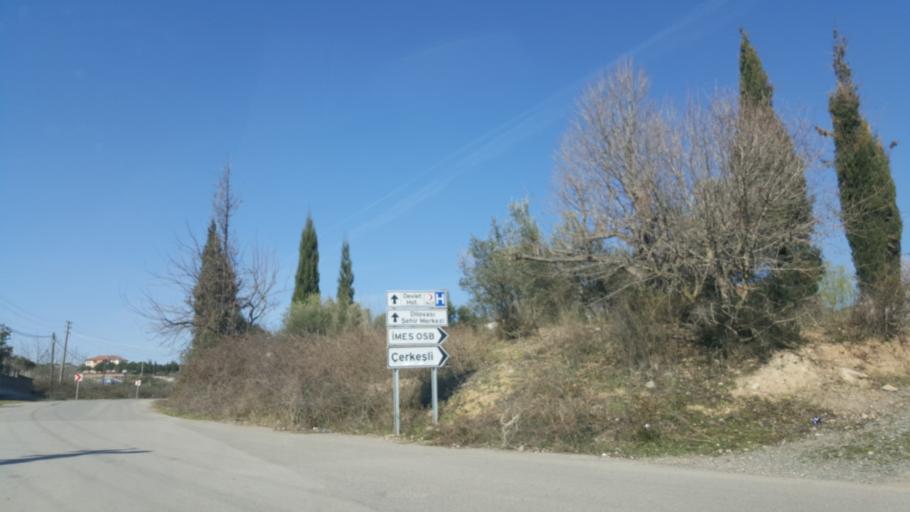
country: TR
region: Kocaeli
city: Tavsancil
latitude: 40.7773
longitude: 29.5752
